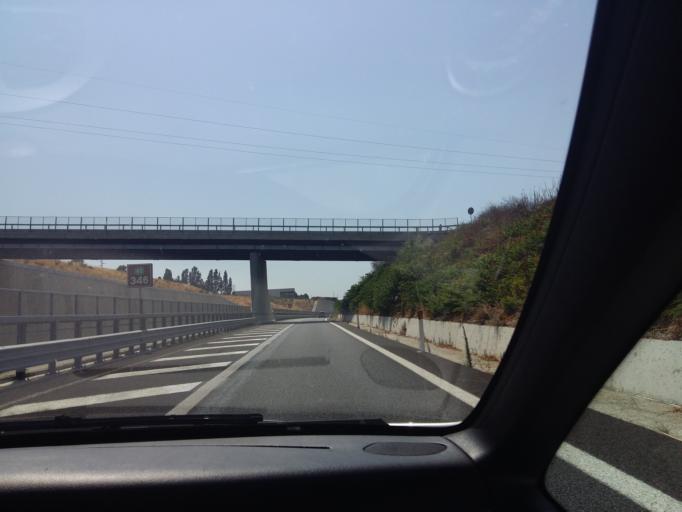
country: IT
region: Calabria
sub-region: Provincia di Reggio Calabria
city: Campo Calabro
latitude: 38.2187
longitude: 15.6478
